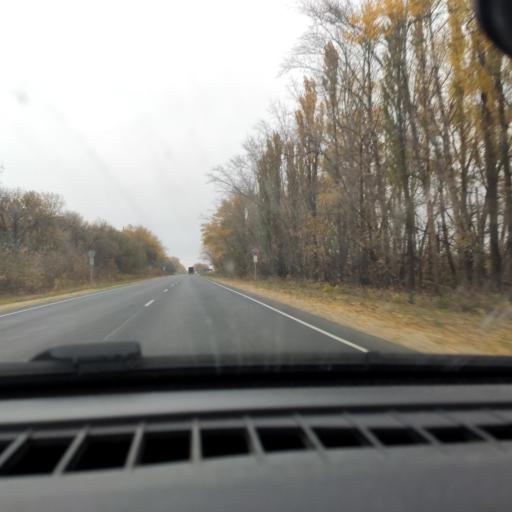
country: RU
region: Voronezj
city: Uryv-Pokrovka
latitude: 51.1664
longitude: 39.0722
